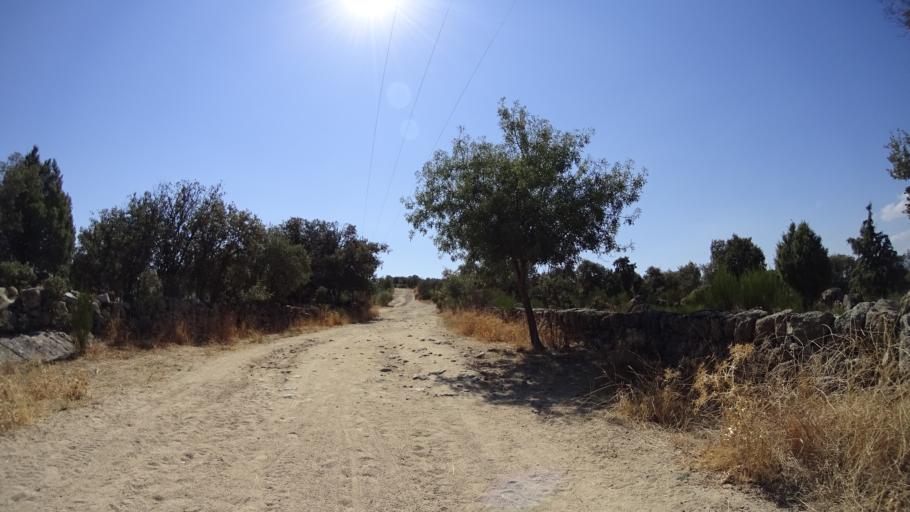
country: ES
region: Madrid
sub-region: Provincia de Madrid
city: Collado-Villalba
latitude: 40.6081
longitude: -4.0112
